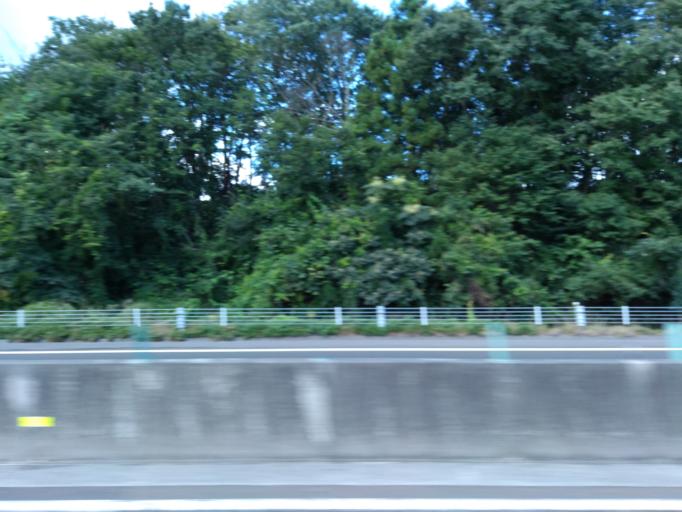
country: JP
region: Miyagi
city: Tomiya
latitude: 38.3359
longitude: 140.8556
